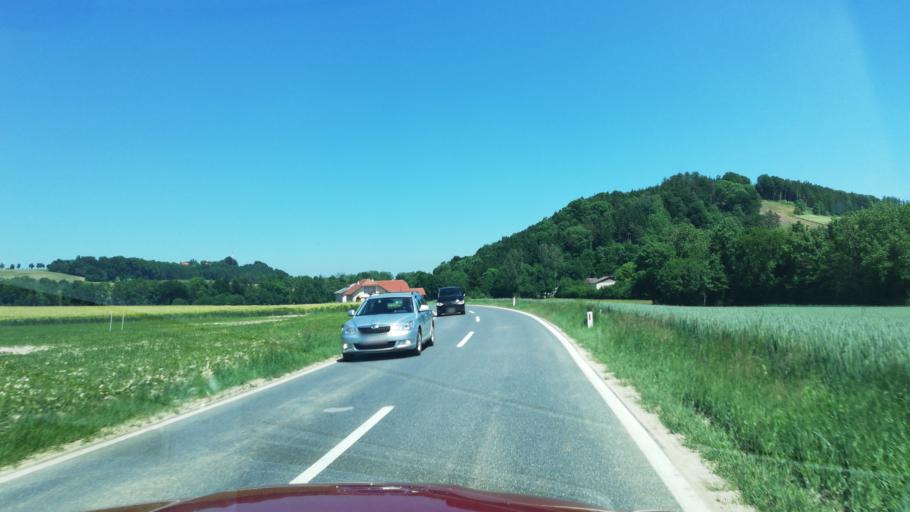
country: AT
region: Upper Austria
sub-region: Wels-Land
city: Bachmanning
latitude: 48.1395
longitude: 13.8052
